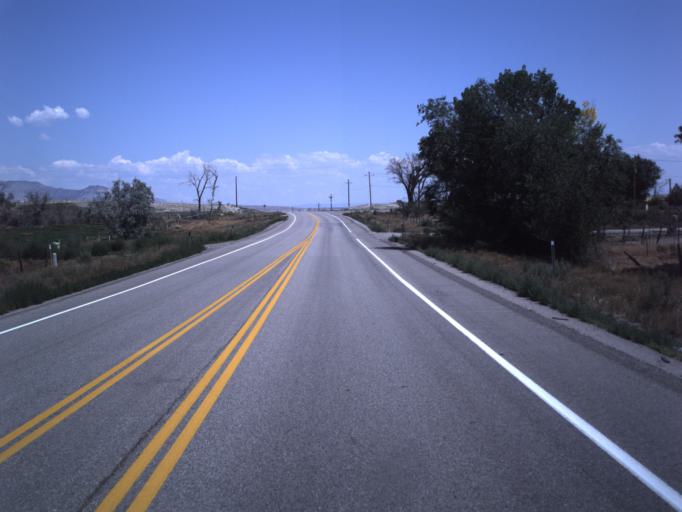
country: US
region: Utah
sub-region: Emery County
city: Ferron
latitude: 39.1359
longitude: -111.0984
